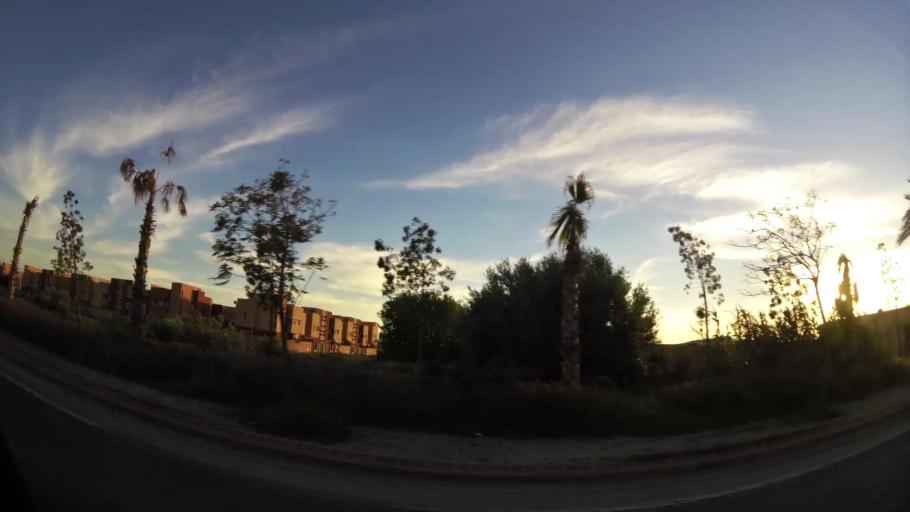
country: MA
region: Marrakech-Tensift-Al Haouz
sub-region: Marrakech
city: Marrakesh
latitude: 31.7646
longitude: -8.1185
